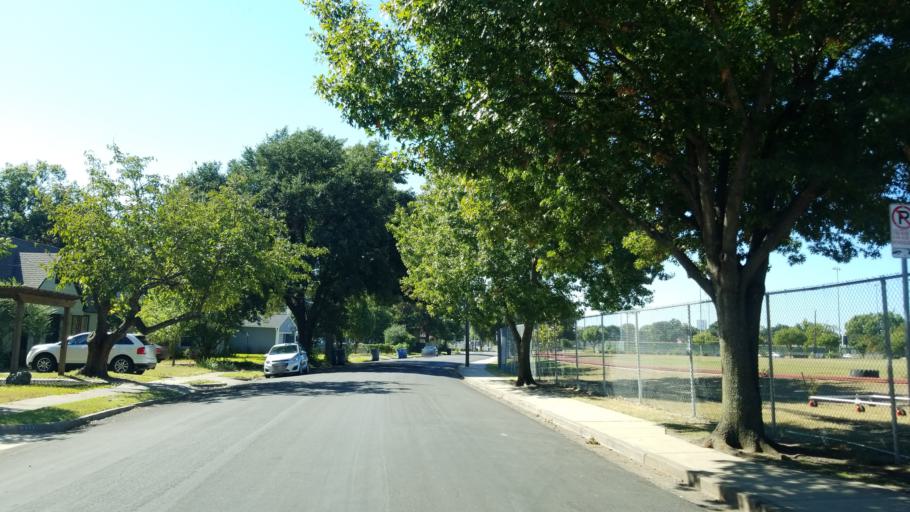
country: US
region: Texas
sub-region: Dallas County
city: Highland Park
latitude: 32.8055
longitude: -96.7487
